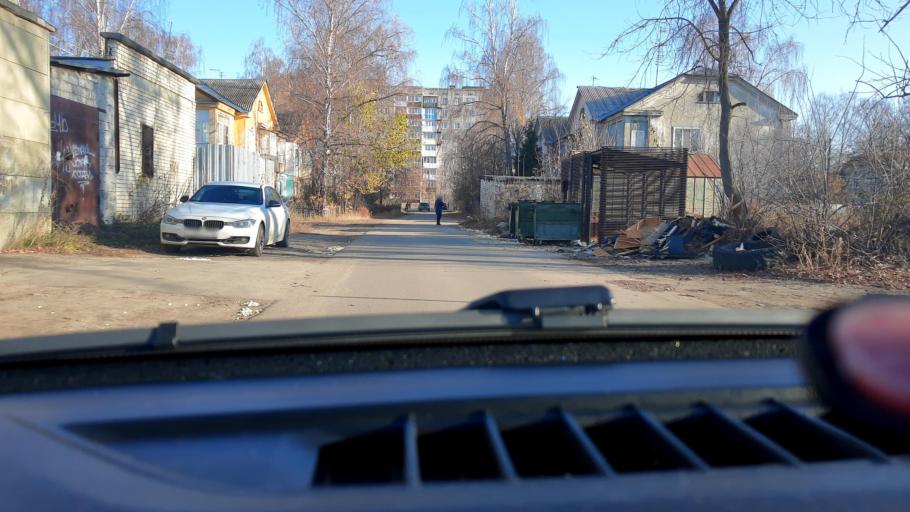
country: RU
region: Nizjnij Novgorod
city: Gorbatovka
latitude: 56.3574
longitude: 43.8426
